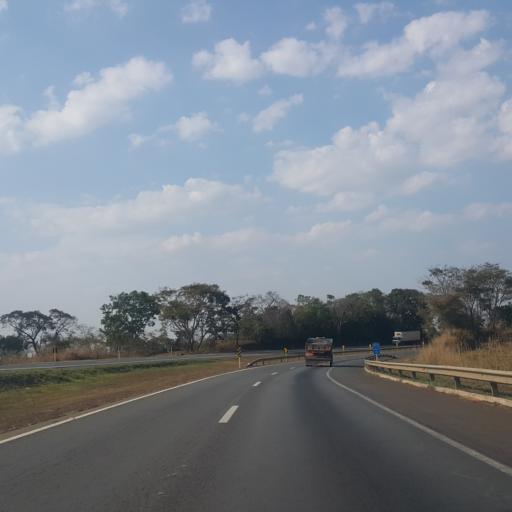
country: BR
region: Goias
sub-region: Abadiania
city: Abadiania
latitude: -16.1648
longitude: -48.6331
